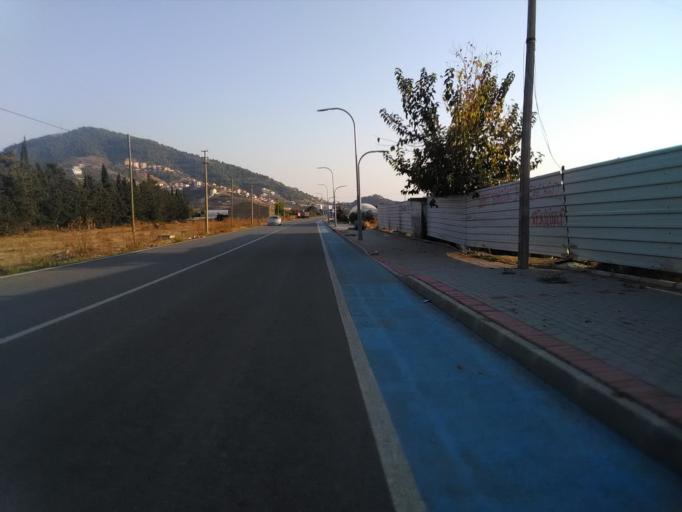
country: TR
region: Antalya
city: Gazipasa
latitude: 36.2507
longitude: 32.2930
